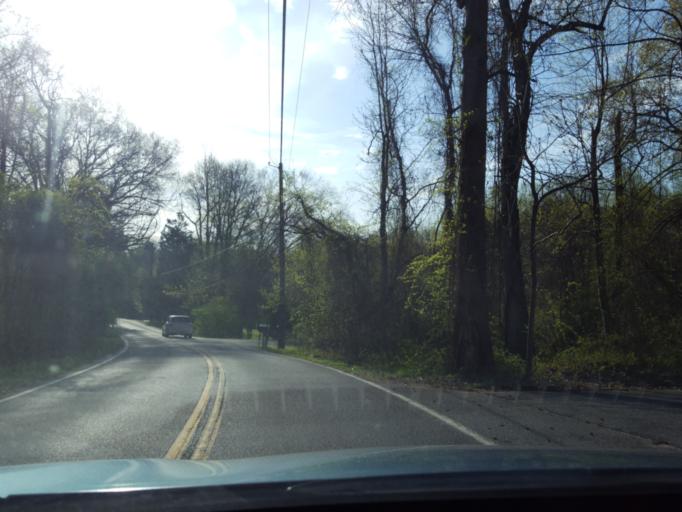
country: US
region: Maryland
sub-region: Prince George's County
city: Croom
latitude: 38.7586
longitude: -76.7336
